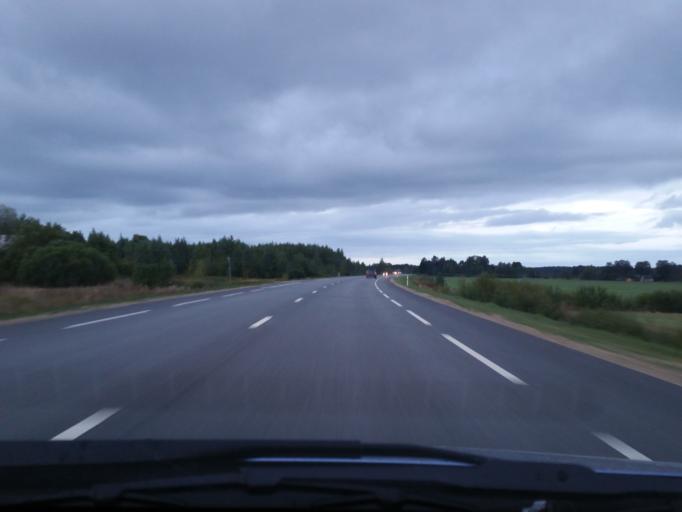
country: LV
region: Adazi
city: Adazi
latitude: 57.1118
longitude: 24.3210
